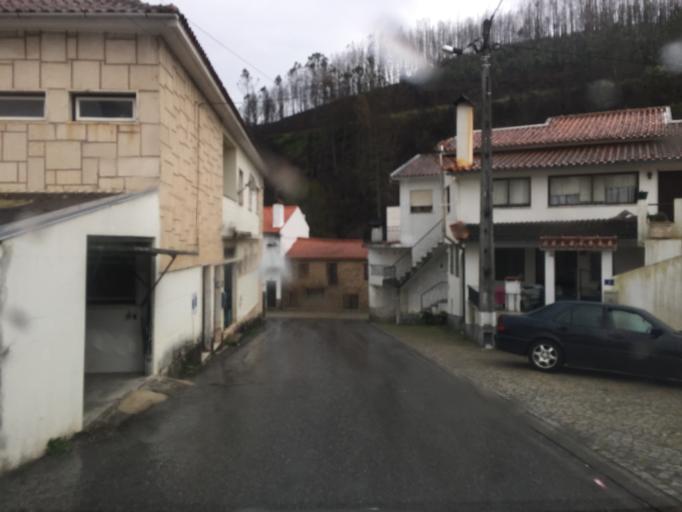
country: PT
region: Leiria
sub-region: Pedrogao Grande
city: Pedrogao Grande
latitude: 40.0170
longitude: -8.0994
